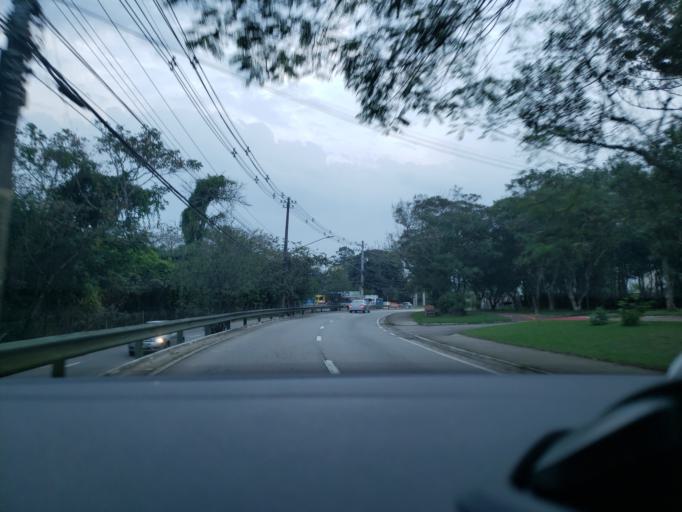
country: BR
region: Sao Paulo
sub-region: Sao Jose Dos Campos
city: Sao Jose dos Campos
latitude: -23.1951
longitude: -45.9284
